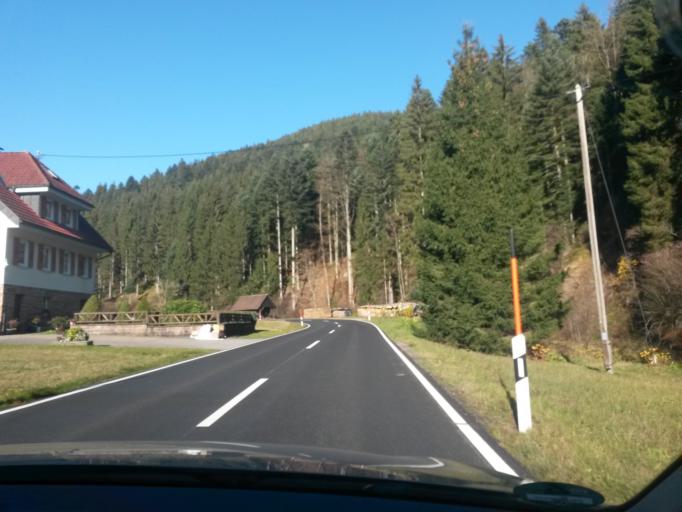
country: DE
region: Baden-Wuerttemberg
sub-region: Karlsruhe Region
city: Bad Rippoldsau-Schapbach
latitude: 48.4420
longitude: 8.3137
